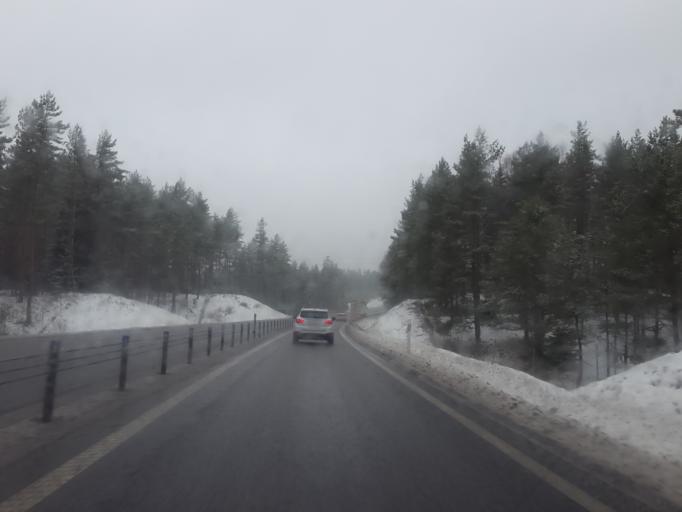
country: SE
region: Joenkoeping
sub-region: Mullsjo Kommun
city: Mullsjoe
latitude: 57.7589
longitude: 13.8408
